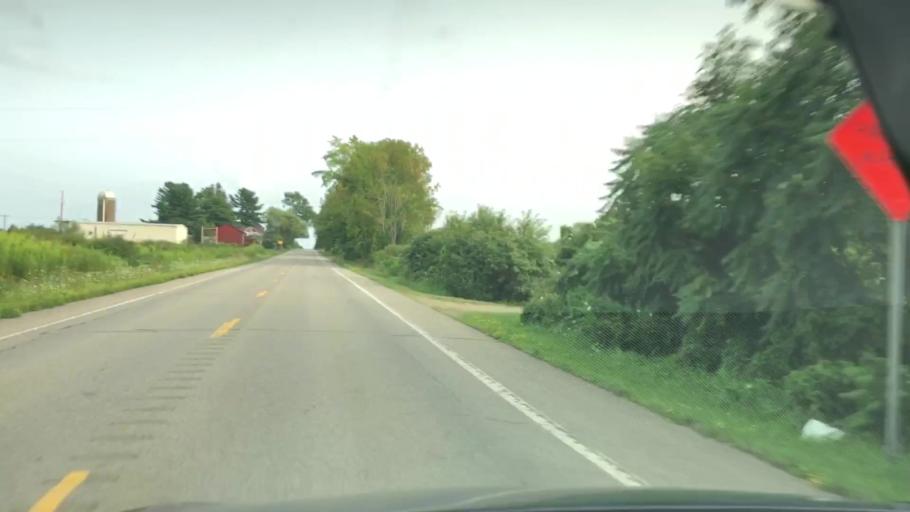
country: US
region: Pennsylvania
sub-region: Erie County
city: Union City
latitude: 41.8125
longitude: -79.8022
